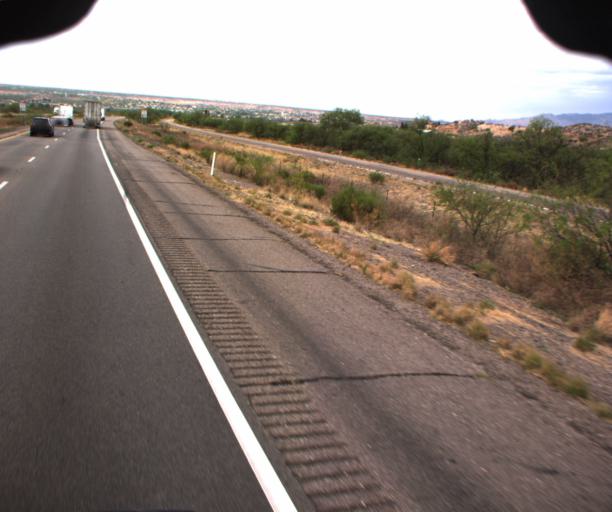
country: US
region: Arizona
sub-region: Cochise County
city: Benson
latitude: 31.9665
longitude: -110.2514
